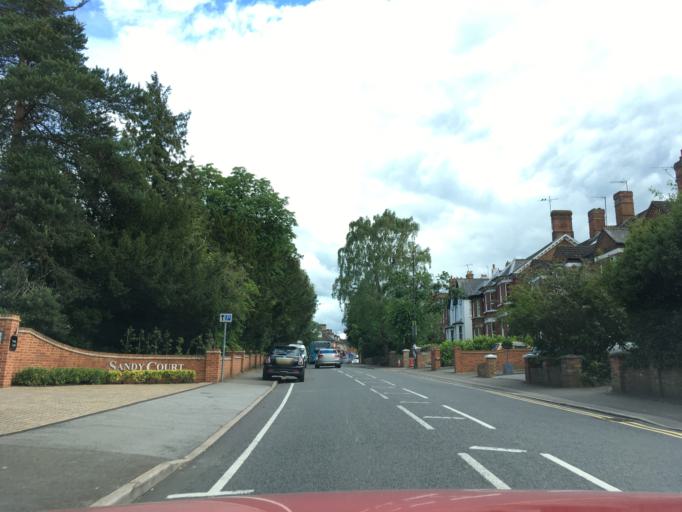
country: GB
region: England
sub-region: Milton Keynes
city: Woburn Sands
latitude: 52.0141
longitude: -0.6486
